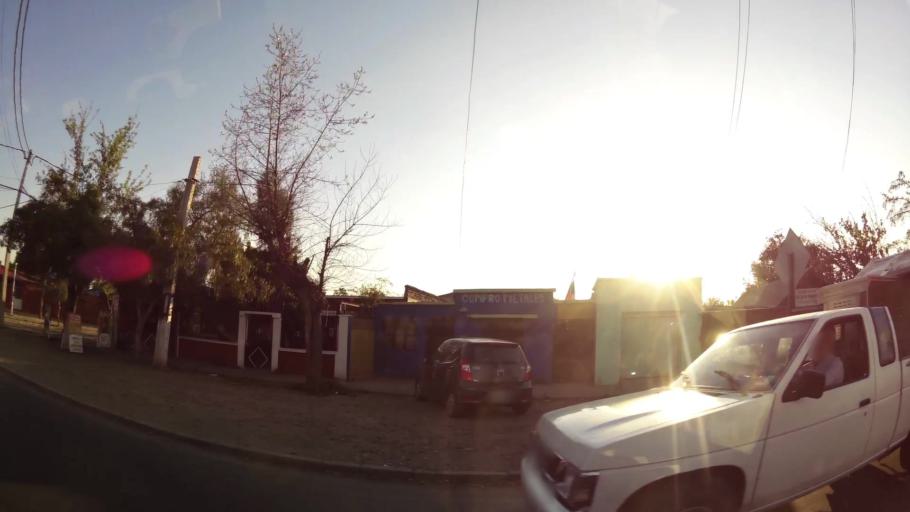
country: CL
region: Santiago Metropolitan
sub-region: Provincia de Santiago
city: La Pintana
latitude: -33.5334
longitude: -70.6224
